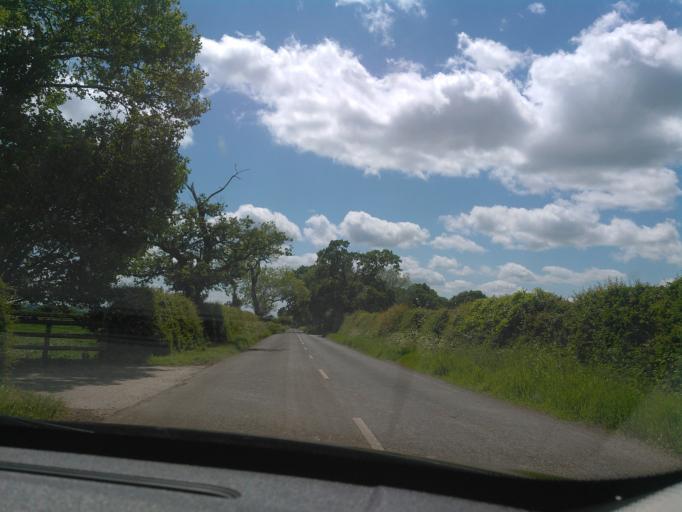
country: GB
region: England
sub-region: Shropshire
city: Wem
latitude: 52.8734
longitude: -2.7177
